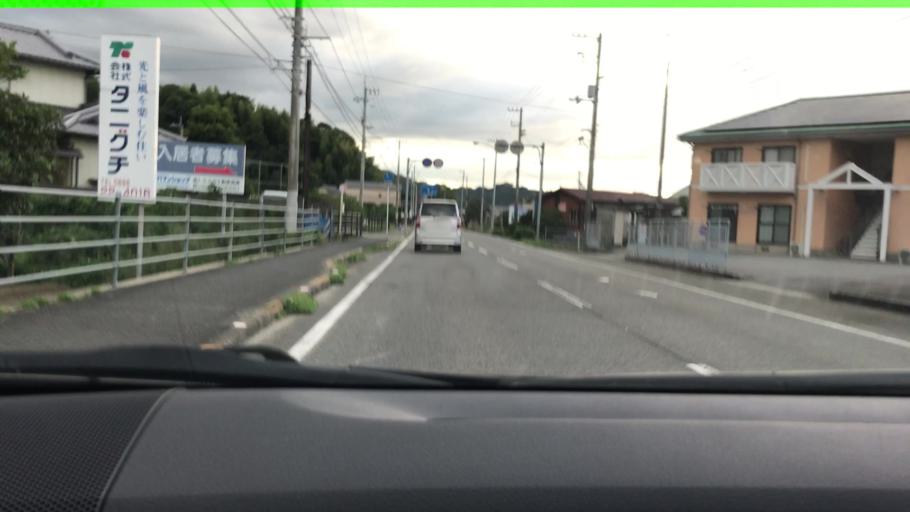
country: JP
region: Ehime
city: Hojo
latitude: 34.0648
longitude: 132.9320
